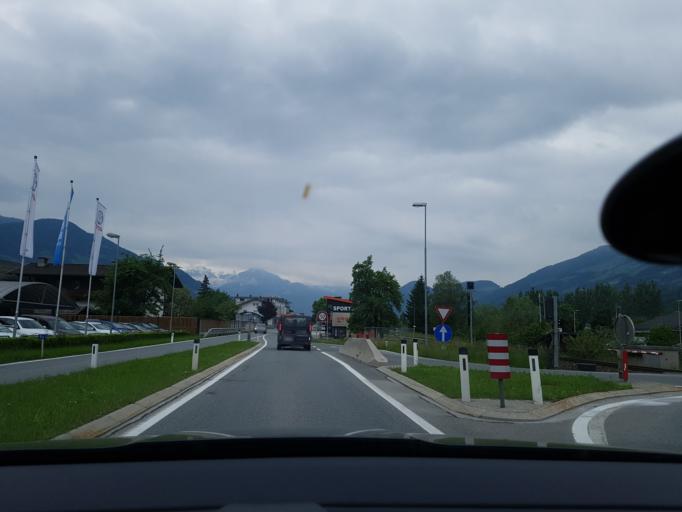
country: AT
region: Tyrol
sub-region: Politischer Bezirk Schwaz
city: Uderns
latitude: 47.3249
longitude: 11.8655
